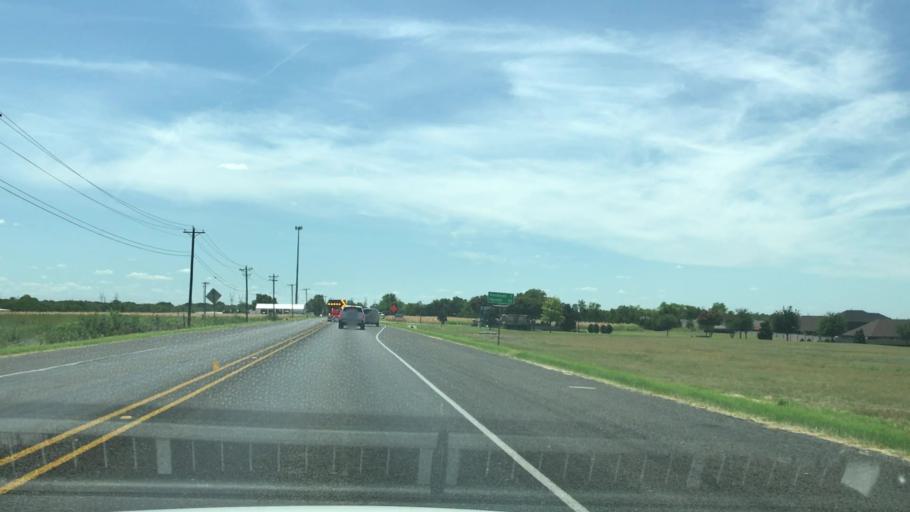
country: US
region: Texas
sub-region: Collin County
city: Lavon
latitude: 33.0200
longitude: -96.4564
